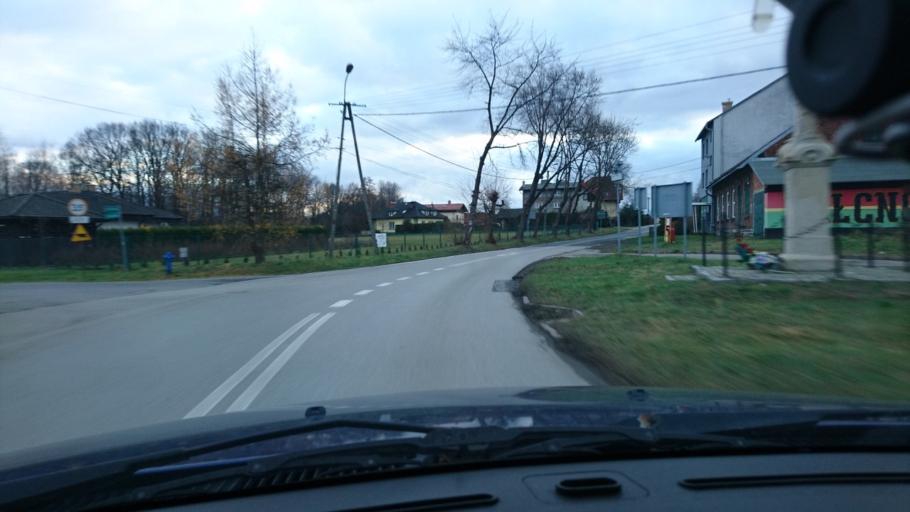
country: PL
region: Silesian Voivodeship
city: Janowice
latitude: 49.8698
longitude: 19.0948
